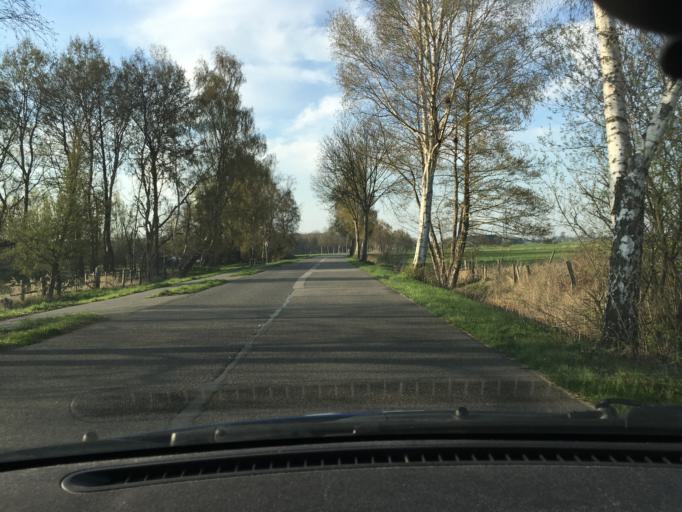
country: DE
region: Lower Saxony
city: Stelle
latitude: 53.4174
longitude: 10.0595
